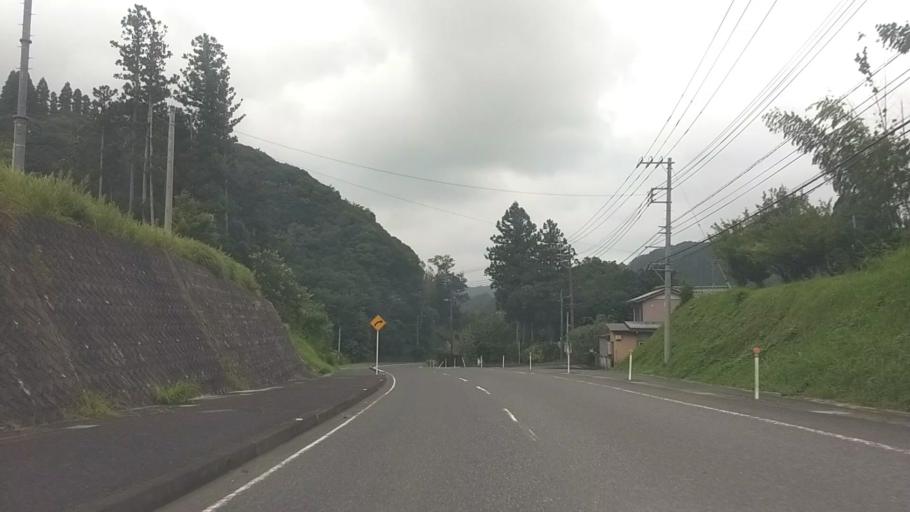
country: JP
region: Chiba
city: Kawaguchi
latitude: 35.2294
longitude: 140.1129
